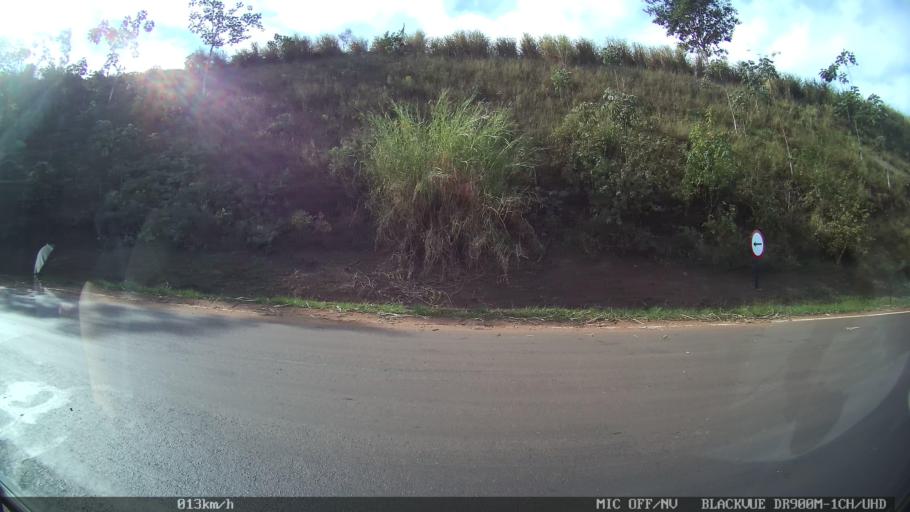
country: BR
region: Sao Paulo
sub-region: Americo Brasiliense
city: Americo Brasiliense
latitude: -21.7532
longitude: -48.0716
